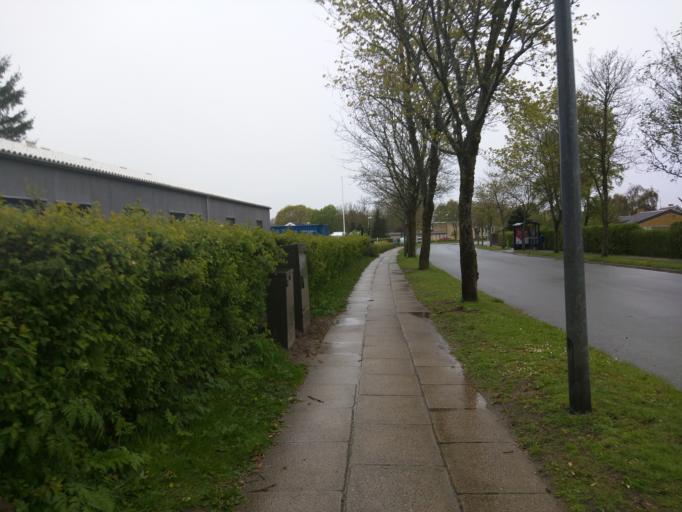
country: DK
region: Central Jutland
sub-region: Viborg Kommune
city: Viborg
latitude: 56.4434
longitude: 9.3788
